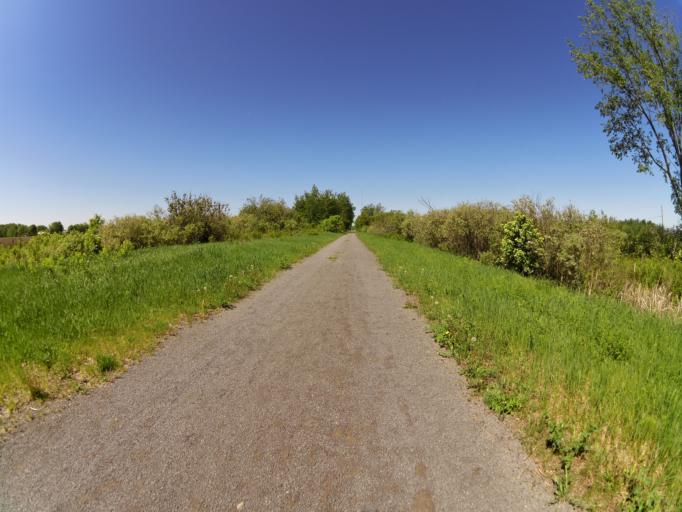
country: CA
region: Ontario
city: Clarence-Rockland
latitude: 45.4227
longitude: -75.3464
